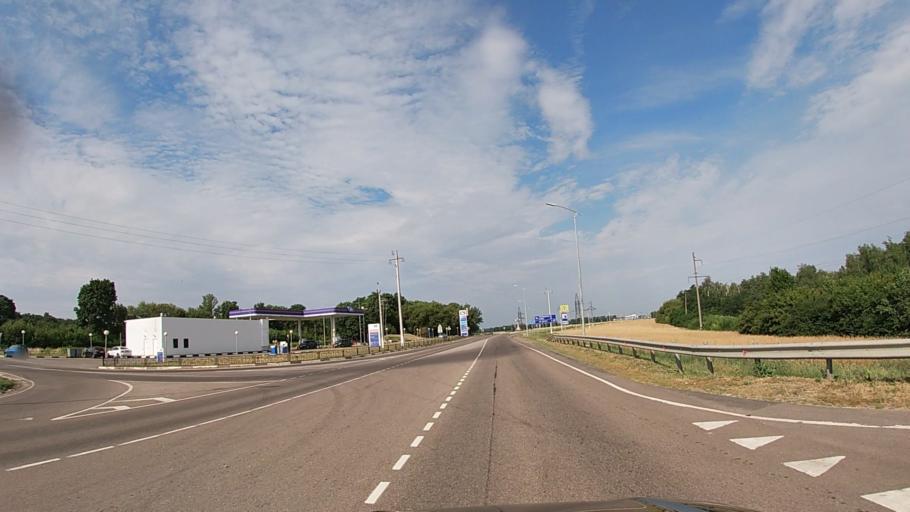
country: RU
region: Belgorod
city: Krasnaya Yaruga
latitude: 50.7969
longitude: 35.7146
